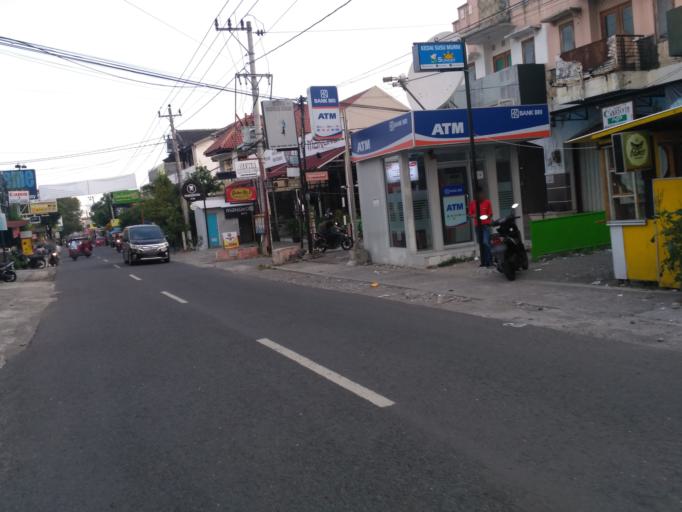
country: ID
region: Daerah Istimewa Yogyakarta
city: Depok
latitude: -7.7656
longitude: 110.4058
